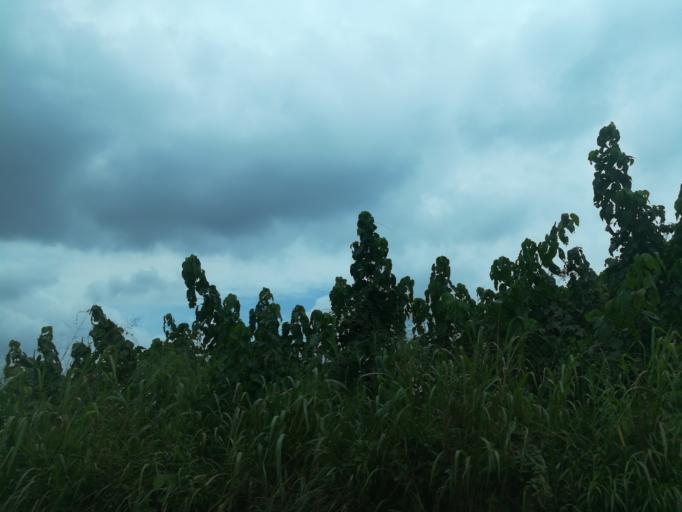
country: NG
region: Lagos
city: Ejirin
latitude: 6.6465
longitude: 3.7211
